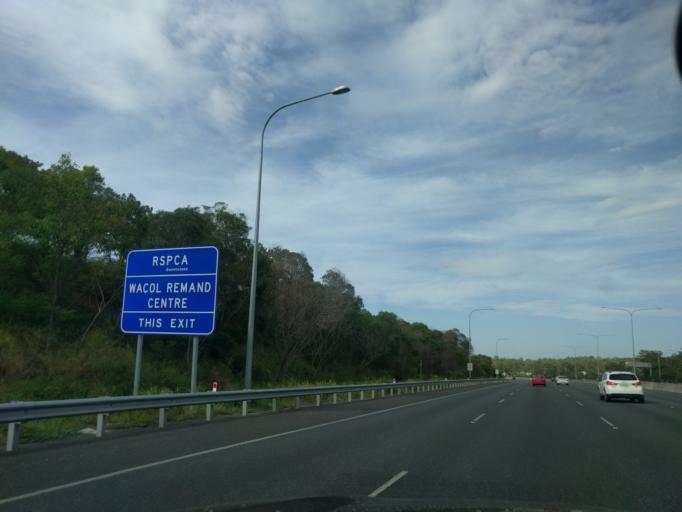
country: AU
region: Queensland
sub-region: Brisbane
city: Wacol
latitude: -27.5828
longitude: 152.9332
